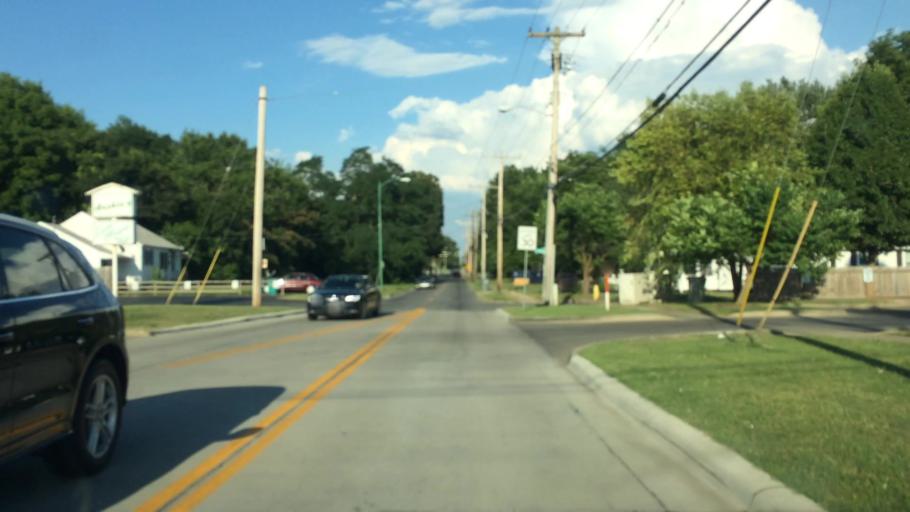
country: US
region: Missouri
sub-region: Greene County
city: Springfield
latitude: 37.1963
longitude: -93.2615
